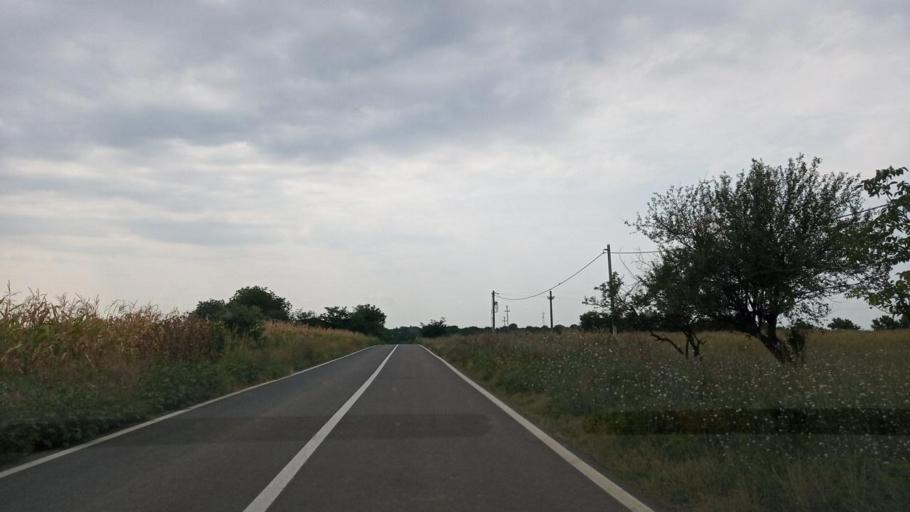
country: RO
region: Giurgiu
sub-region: Comuna Gostinari
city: Gostinari
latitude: 44.1678
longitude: 26.2585
